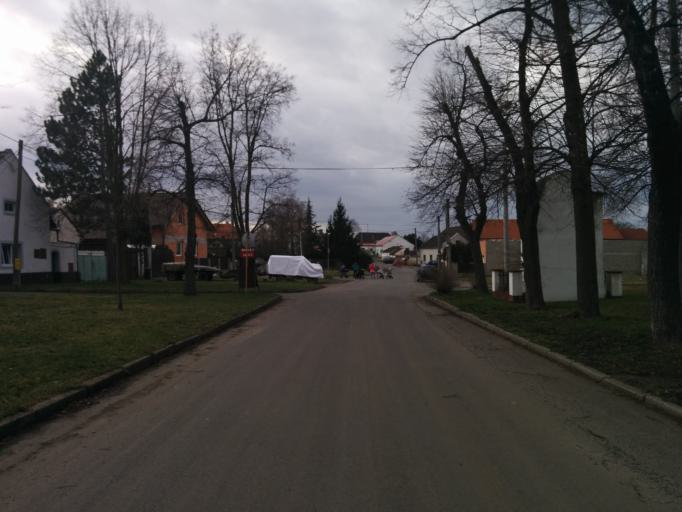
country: CZ
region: Central Bohemia
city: Libis
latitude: 50.2794
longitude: 14.5022
